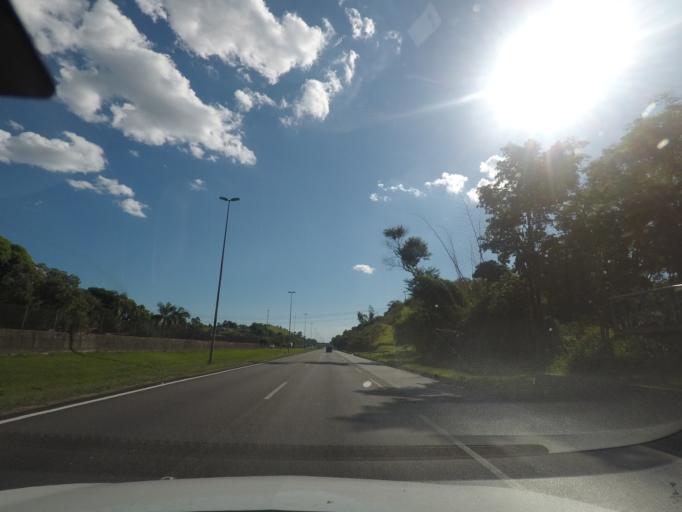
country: BR
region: Rio de Janeiro
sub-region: Guapimirim
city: Guapimirim
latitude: -22.6066
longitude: -43.0280
